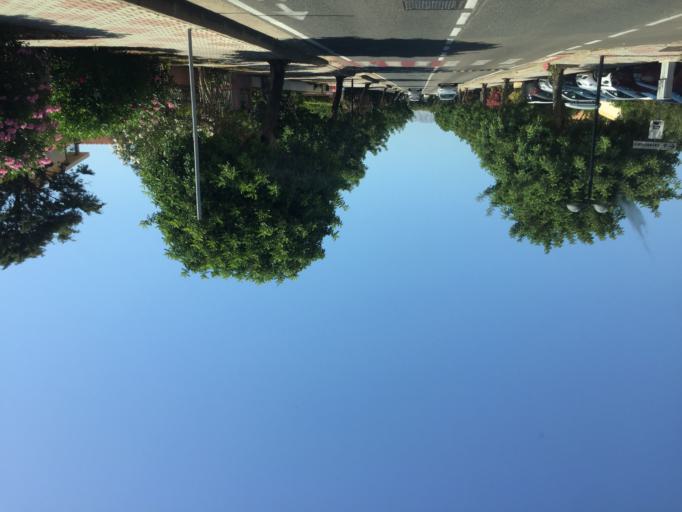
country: IT
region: Sardinia
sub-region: Provincia di Olbia-Tempio
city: San Teodoro
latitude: 40.7789
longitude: 9.6679
